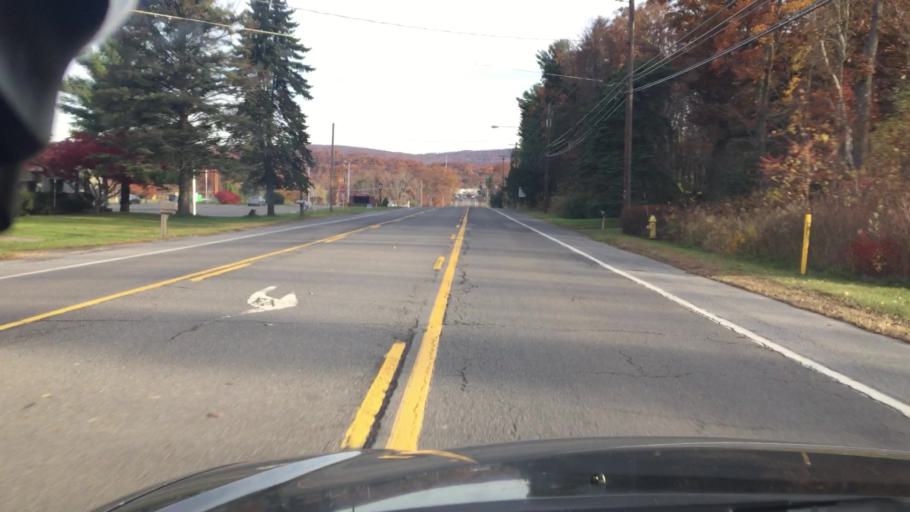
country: US
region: Pennsylvania
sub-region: Luzerne County
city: Mountain Top
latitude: 41.1378
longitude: -75.9024
